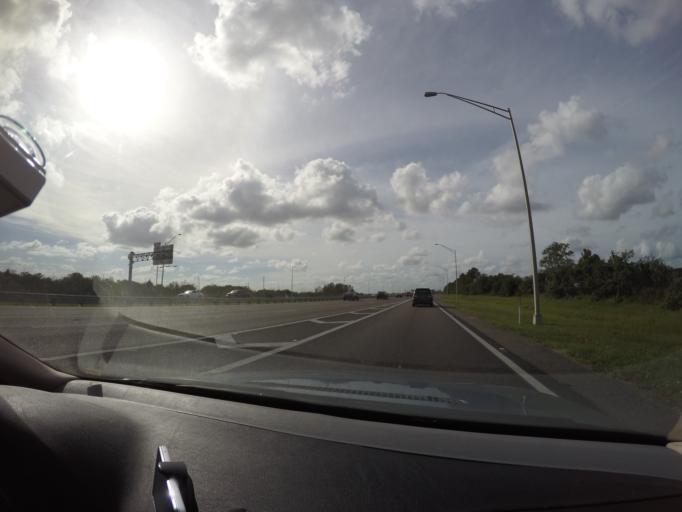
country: US
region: Florida
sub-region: Orange County
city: Conway
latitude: 28.4488
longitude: -81.2695
